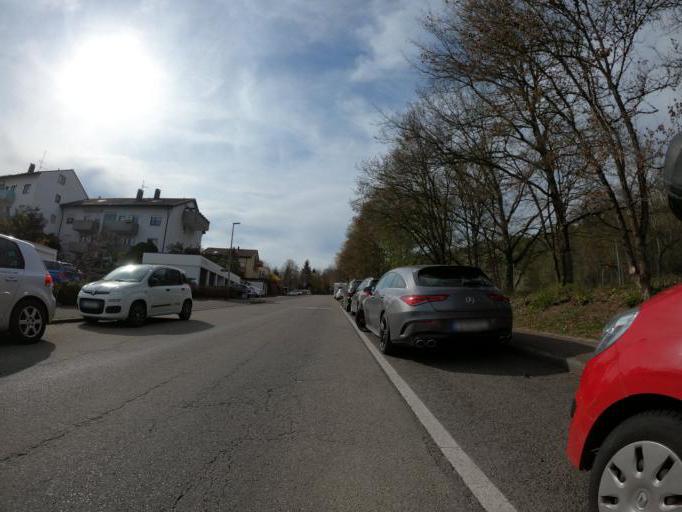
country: DE
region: Baden-Wuerttemberg
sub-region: Regierungsbezirk Stuttgart
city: Stuttgart-Ost
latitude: 48.7565
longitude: 9.2190
